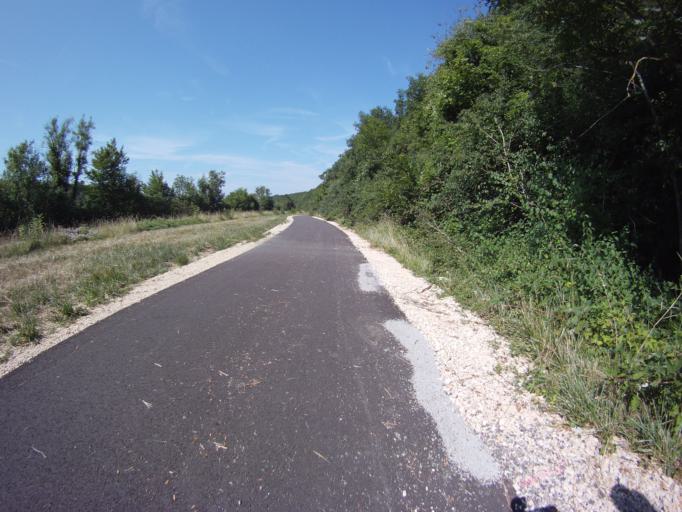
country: FR
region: Lorraine
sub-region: Departement de Meurthe-et-Moselle
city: Saizerais
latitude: 48.7552
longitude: 6.0200
